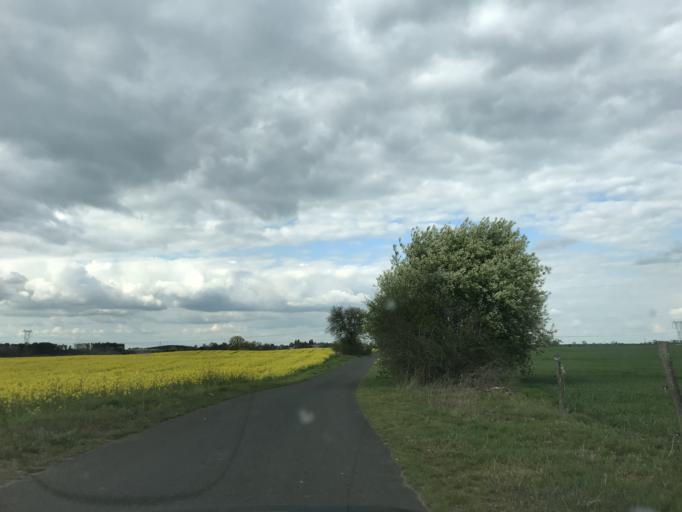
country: PL
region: West Pomeranian Voivodeship
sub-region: Powiat mysliborski
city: Mysliborz
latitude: 52.8774
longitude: 14.8933
